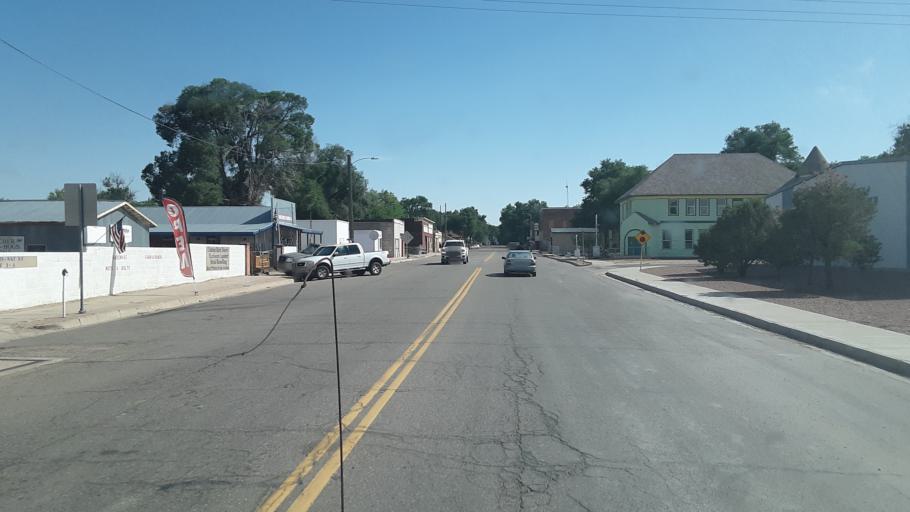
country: US
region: Colorado
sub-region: Crowley County
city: Ordway
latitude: 38.1094
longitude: -103.8660
